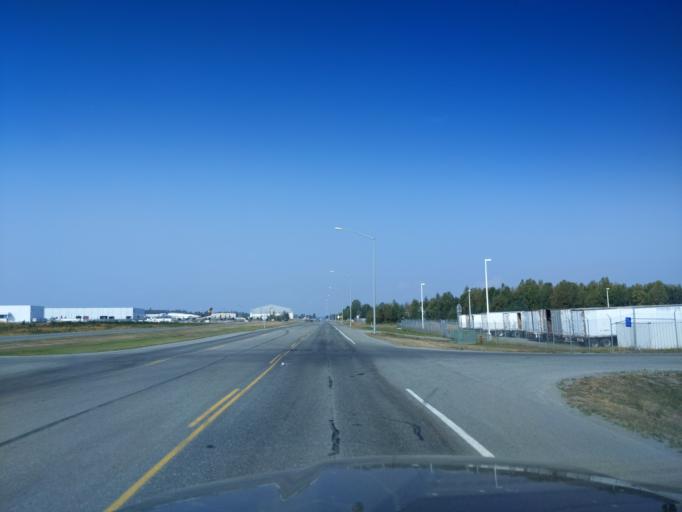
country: US
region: Alaska
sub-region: Anchorage Municipality
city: Anchorage
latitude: 61.1852
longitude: -149.9888
